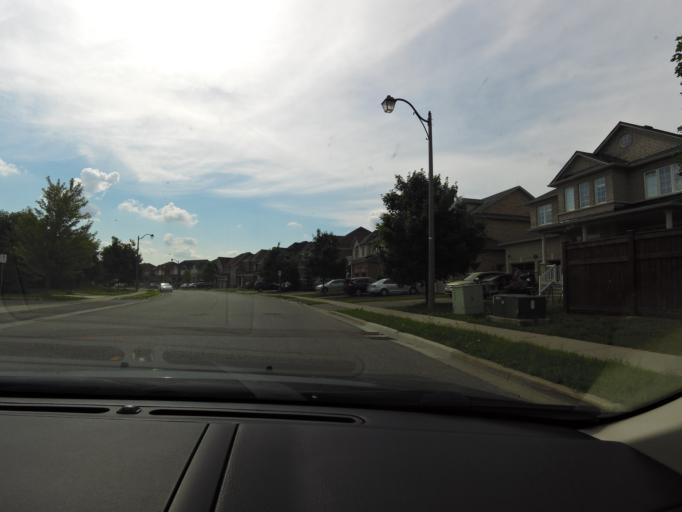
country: CA
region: Ontario
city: Brampton
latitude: 43.7894
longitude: -79.7489
